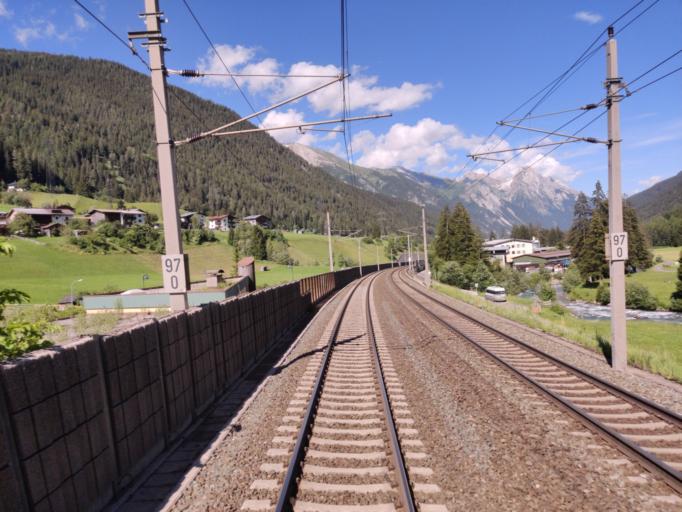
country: AT
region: Tyrol
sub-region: Politischer Bezirk Landeck
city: Sankt Anton am Arlberg
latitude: 47.1401
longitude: 10.2913
